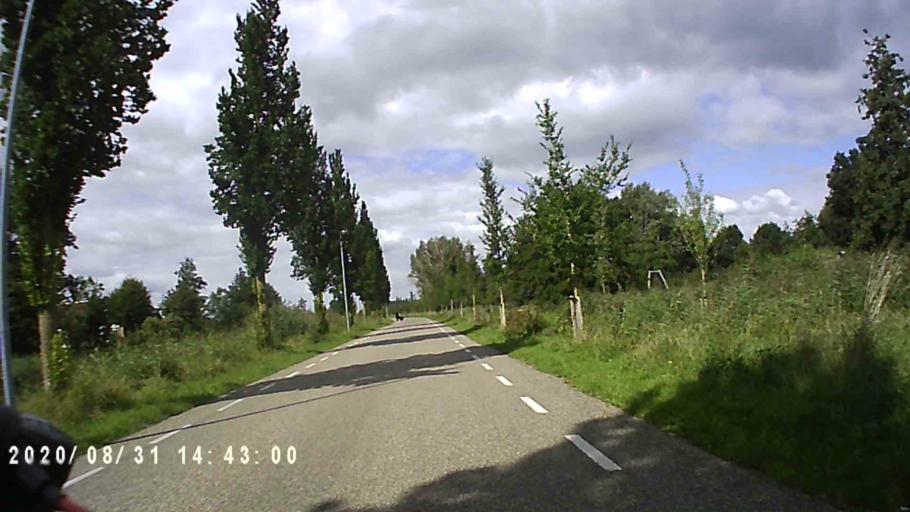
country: NL
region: Groningen
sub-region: Gemeente Zuidhorn
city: Zuidhorn
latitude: 53.2461
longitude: 6.3862
